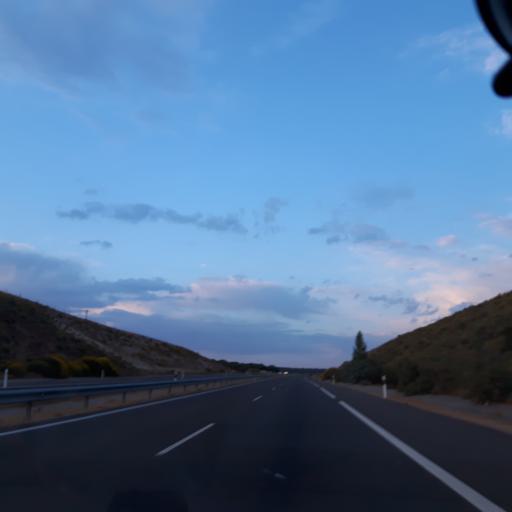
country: ES
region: Castille and Leon
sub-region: Provincia de Salamanca
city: Mozarbez
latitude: 40.8439
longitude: -5.6399
